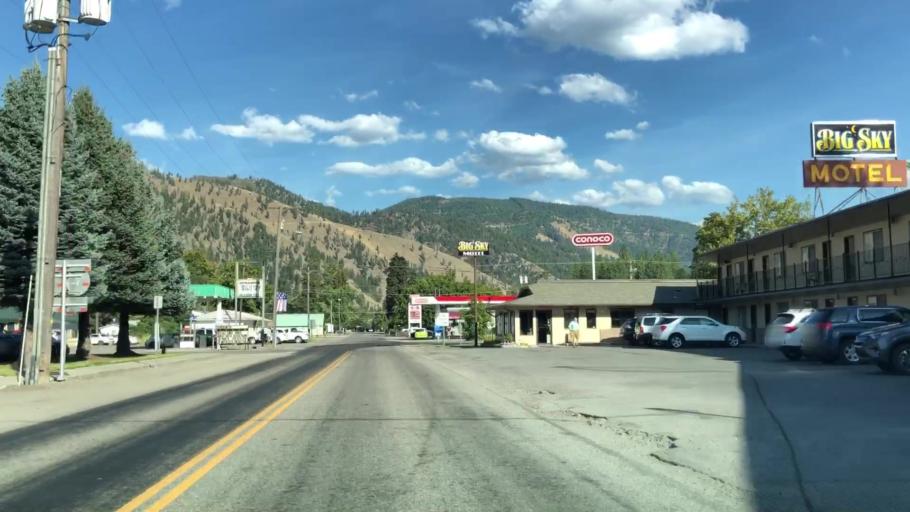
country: US
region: Montana
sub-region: Mineral County
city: Superior
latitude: 47.1925
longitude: -114.8905
